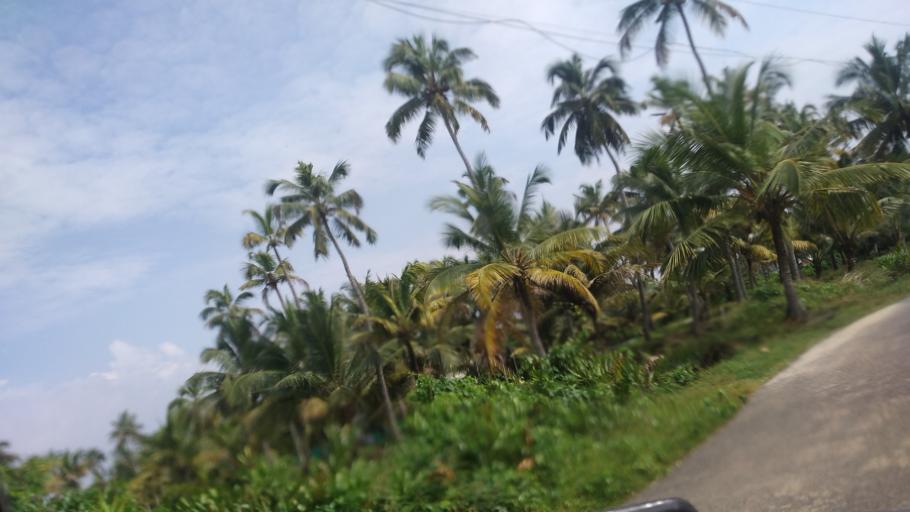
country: IN
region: Kerala
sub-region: Ernakulam
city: Elur
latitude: 10.0870
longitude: 76.1959
